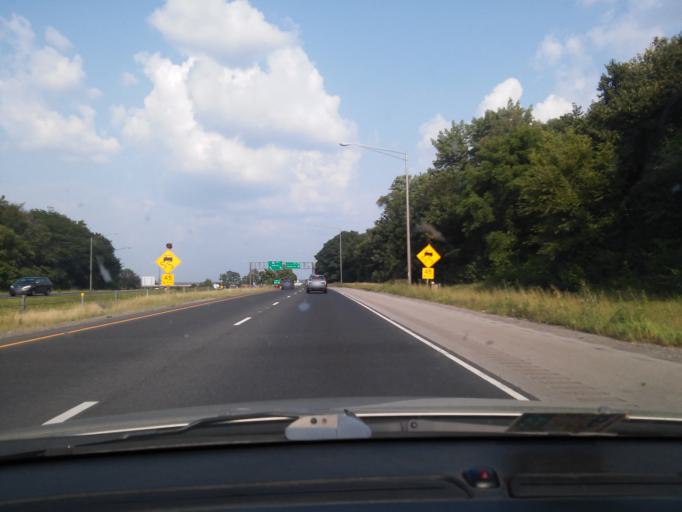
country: US
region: Illinois
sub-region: Will County
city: Rockdale
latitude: 41.5117
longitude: -88.1042
